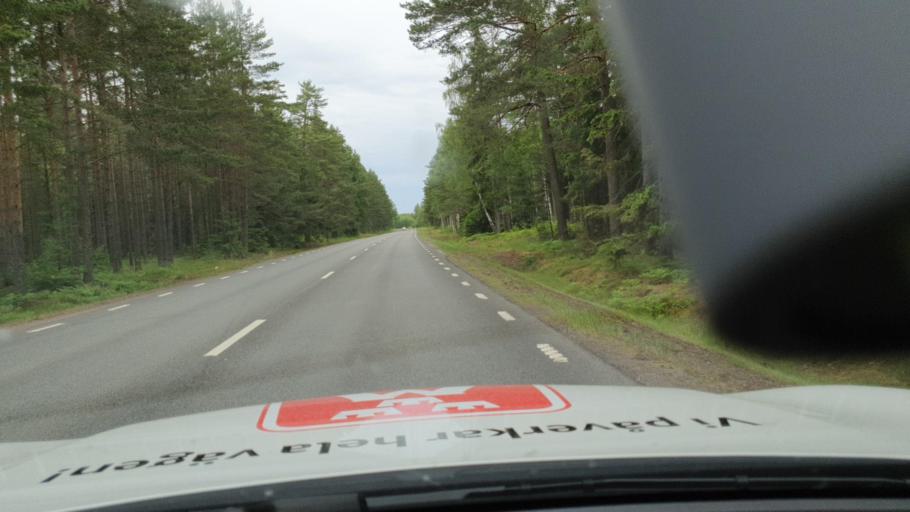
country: SE
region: Vaestra Goetaland
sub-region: Karlsborgs Kommun
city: Molltorp
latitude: 58.4655
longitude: 14.4052
